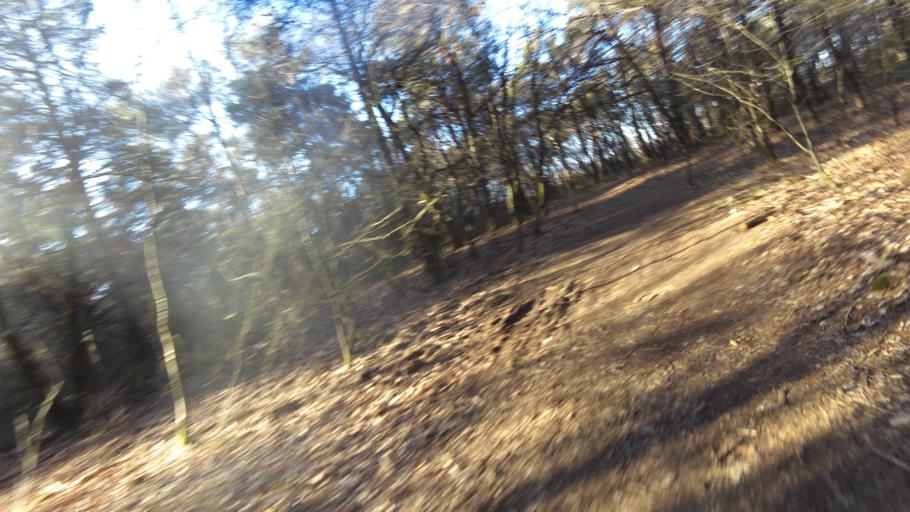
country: NL
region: Gelderland
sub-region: Gemeente Barneveld
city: Garderen
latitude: 52.2764
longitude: 5.6952
